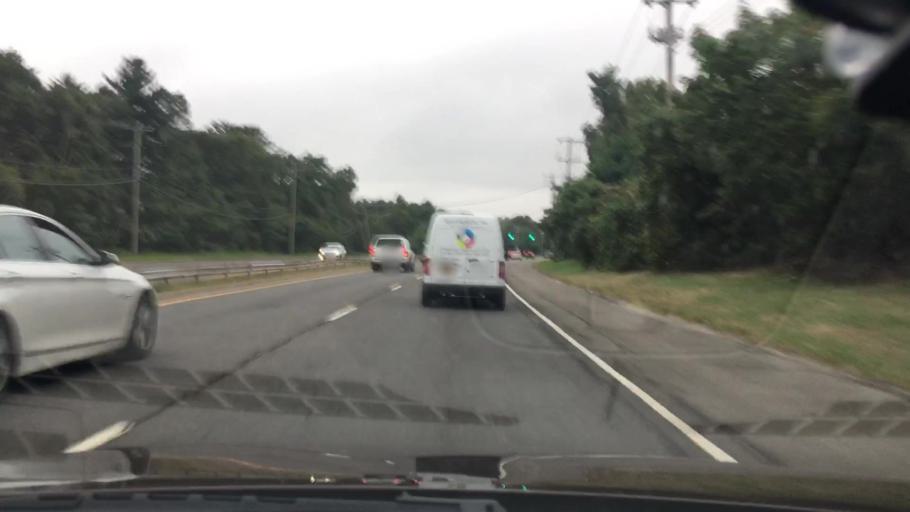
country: US
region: New York
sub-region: Suffolk County
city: Nesconset
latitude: 40.8565
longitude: -73.1428
